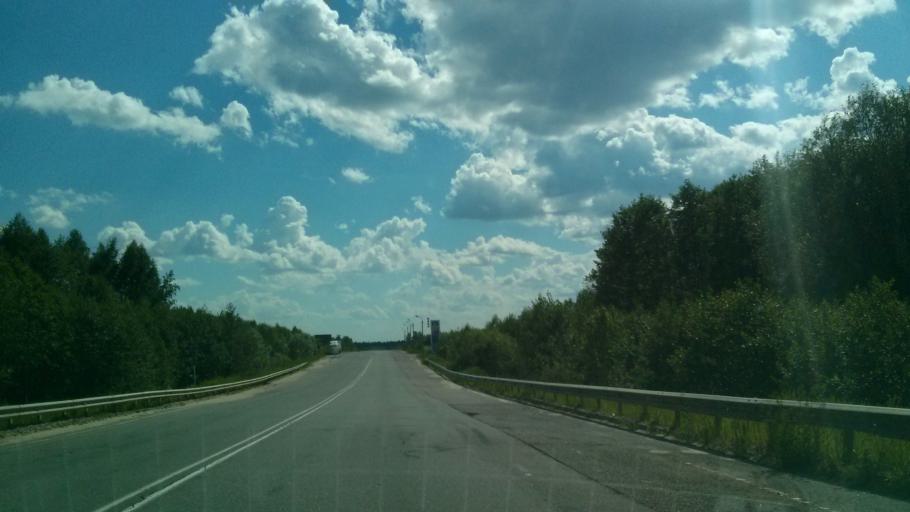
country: RU
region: Vladimir
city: Melenki
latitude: 55.3405
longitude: 41.6677
